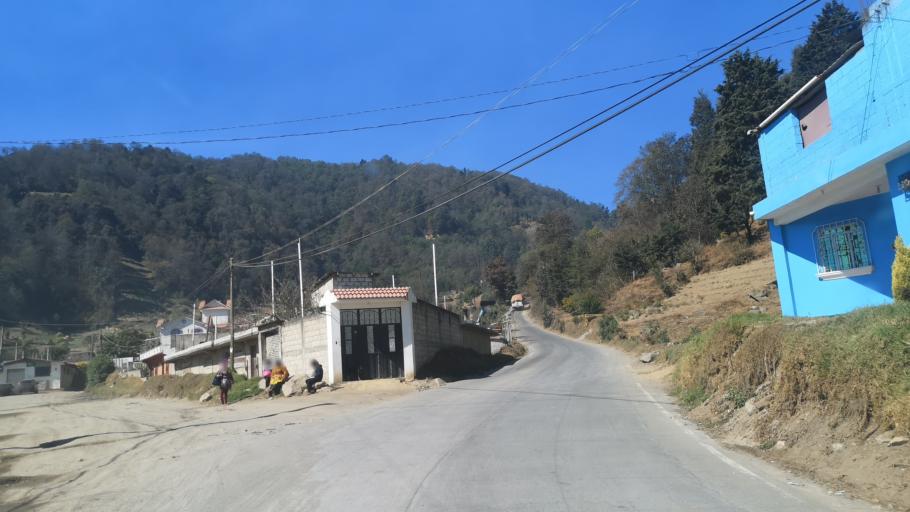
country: GT
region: Quetzaltenango
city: Quetzaltenango
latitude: 14.7941
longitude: -91.5524
